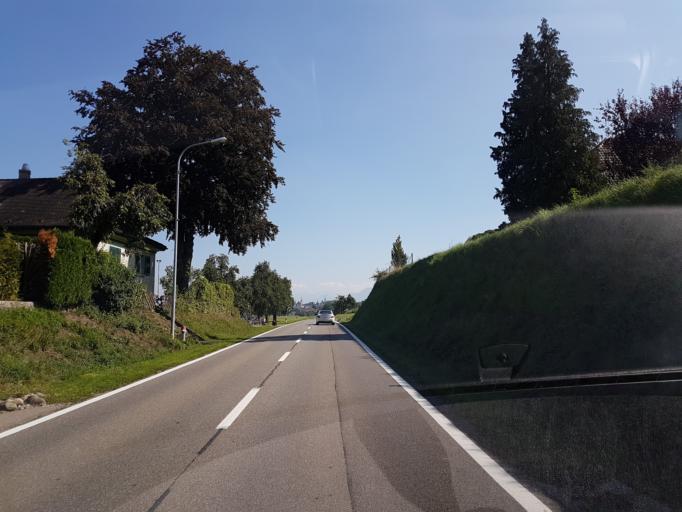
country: CH
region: Aargau
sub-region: Bezirk Muri
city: Muri
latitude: 47.2938
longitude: 8.3205
